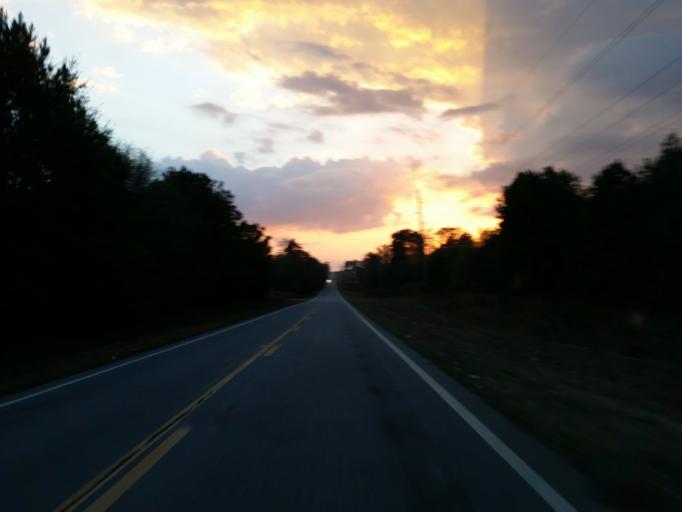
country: US
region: Georgia
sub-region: Dooly County
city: Unadilla
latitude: 32.1581
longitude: -83.6385
